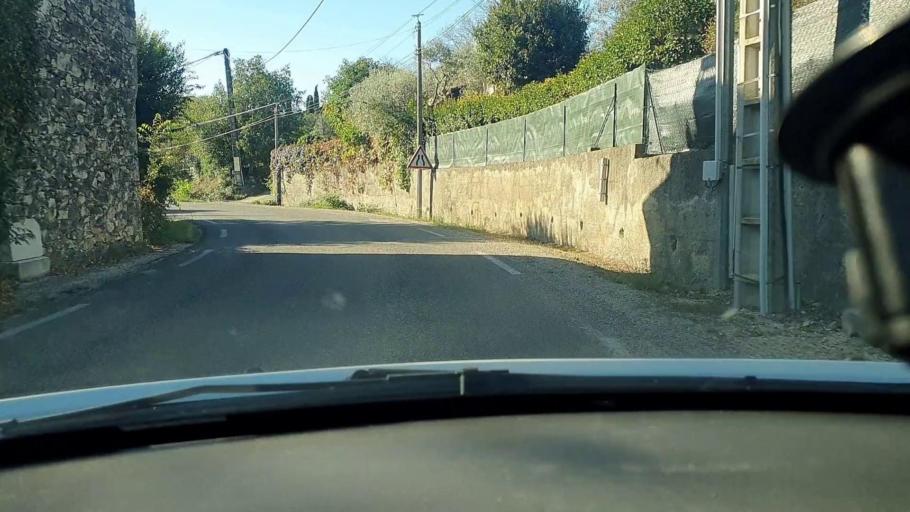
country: FR
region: Languedoc-Roussillon
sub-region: Departement du Gard
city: Goudargues
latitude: 44.2307
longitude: 4.4454
